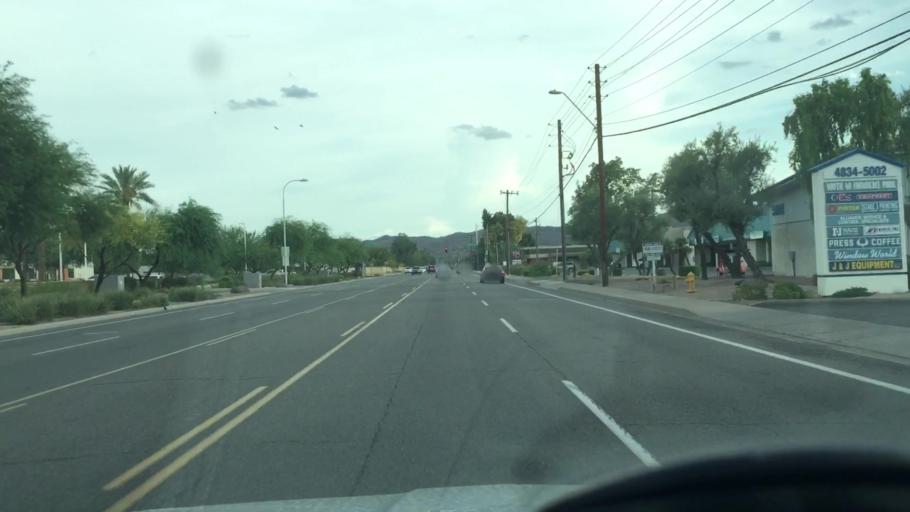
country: US
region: Arizona
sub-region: Maricopa County
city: Guadalupe
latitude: 33.4018
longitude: -111.9954
